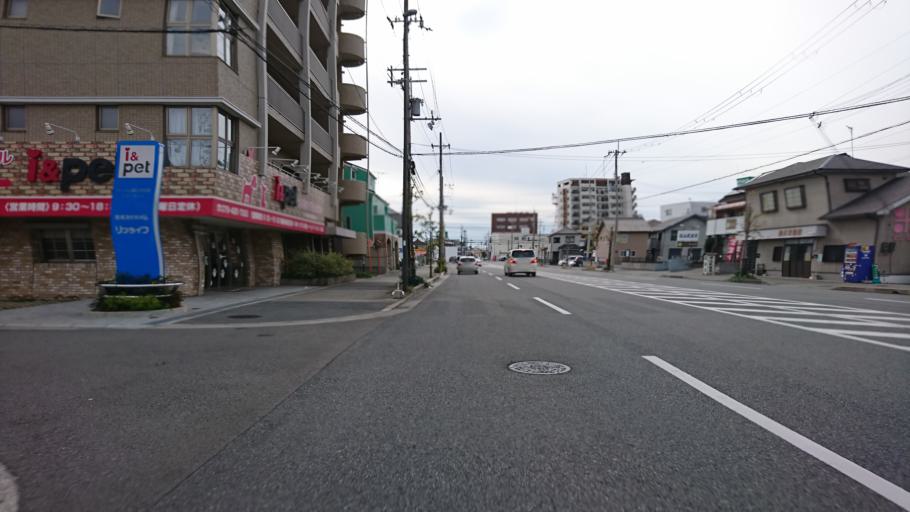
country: JP
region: Hyogo
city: Kakogawacho-honmachi
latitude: 34.7628
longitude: 134.8441
